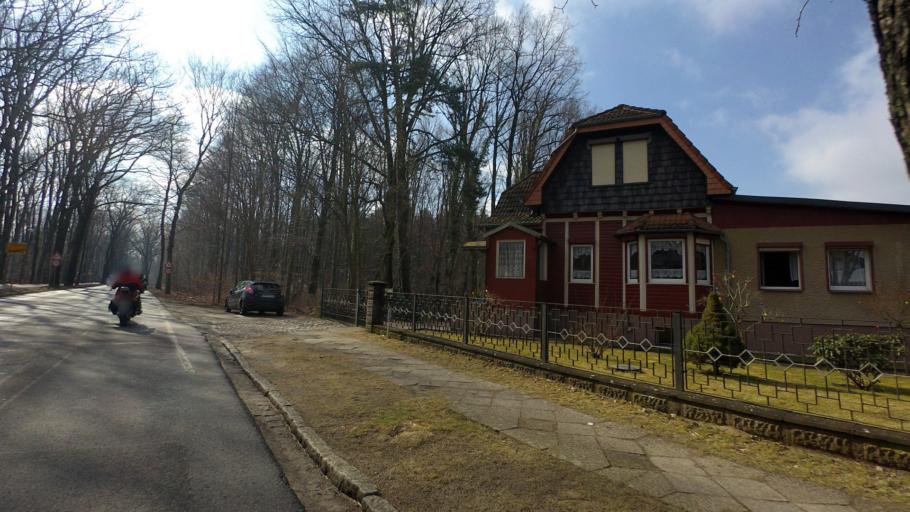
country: DE
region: Brandenburg
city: Glienicke
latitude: 52.6663
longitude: 13.3212
